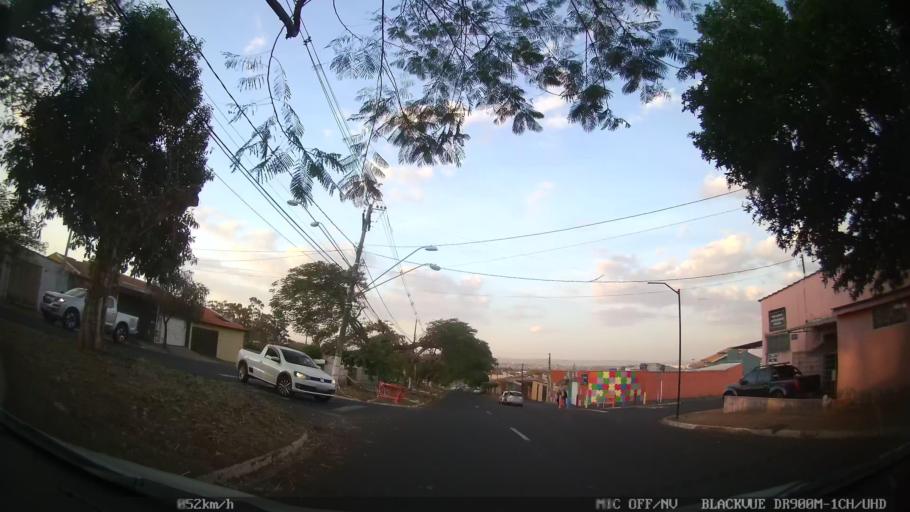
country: BR
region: Sao Paulo
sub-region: Ribeirao Preto
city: Ribeirao Preto
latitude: -21.1336
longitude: -47.8435
